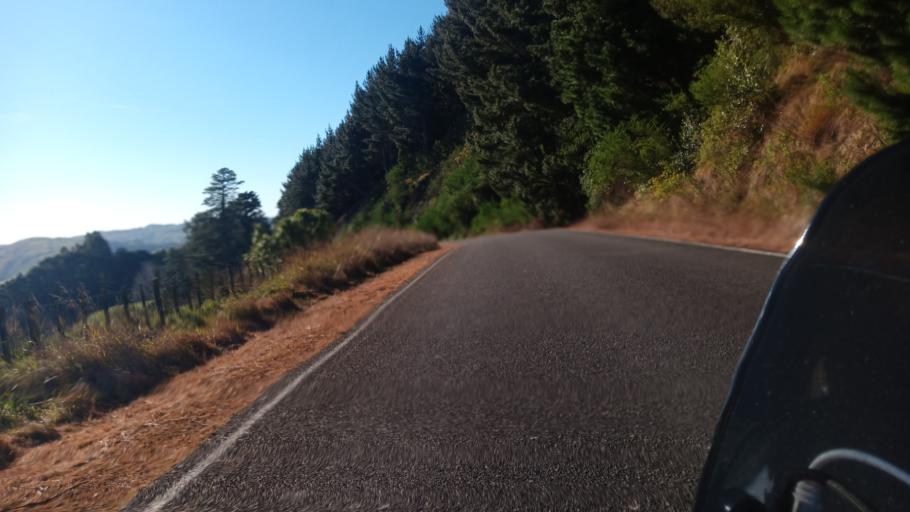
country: NZ
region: Hawke's Bay
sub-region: Wairoa District
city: Wairoa
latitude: -38.8307
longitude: 177.2859
